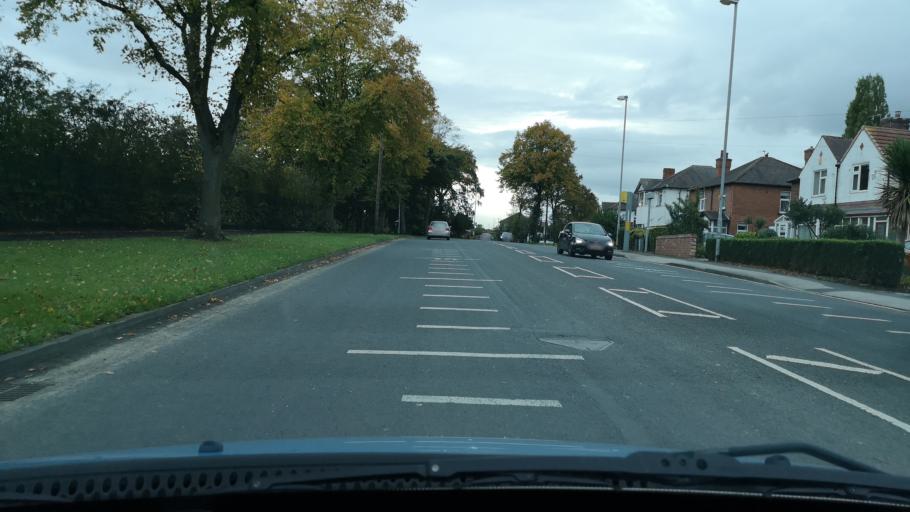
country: GB
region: England
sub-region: City and Borough of Wakefield
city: Crigglestone
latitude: 53.6696
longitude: -1.5273
